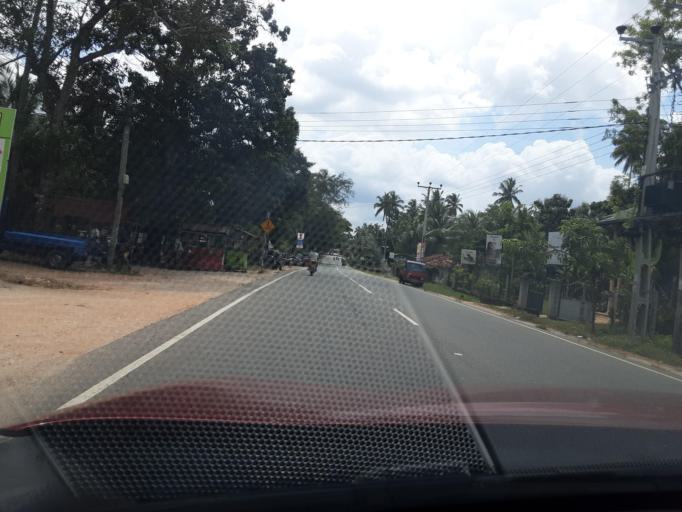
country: LK
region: North Western
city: Kuliyapitiya
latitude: 7.4507
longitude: 80.1834
